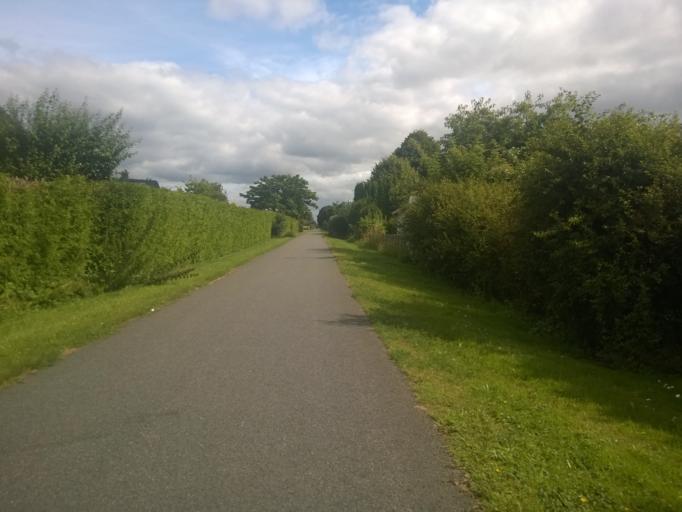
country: SE
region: Skane
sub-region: Kristianstads Kommun
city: Kristianstad
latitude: 56.0530
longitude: 14.1717
